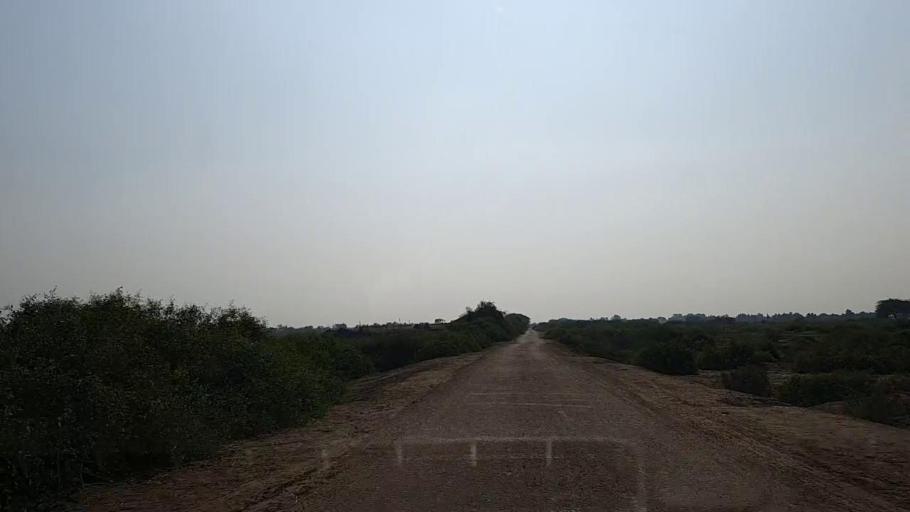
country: PK
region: Sindh
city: Mirpur Sakro
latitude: 24.6351
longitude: 67.6599
